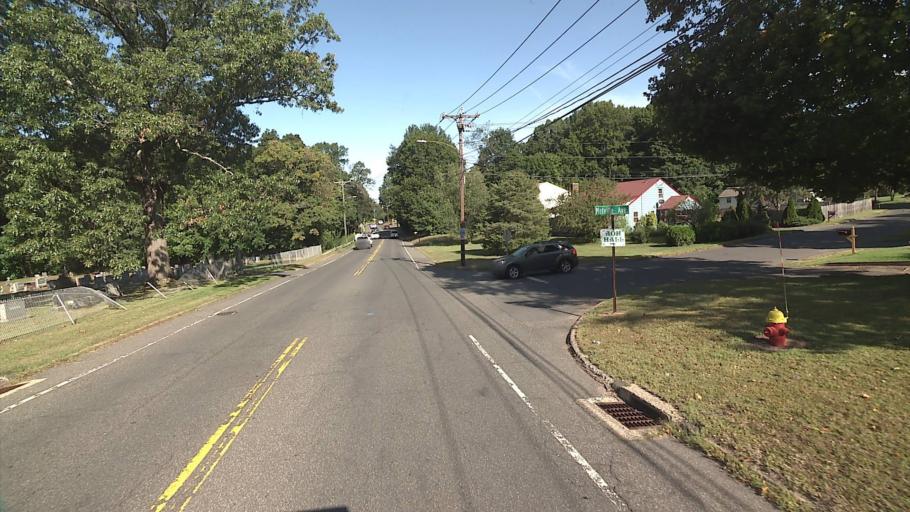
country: US
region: Connecticut
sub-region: New Haven County
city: Meriden
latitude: 41.5123
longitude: -72.8214
